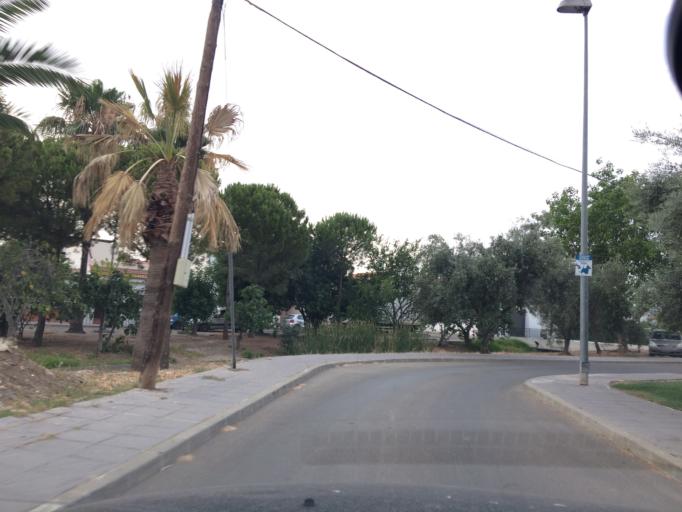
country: ES
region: Andalusia
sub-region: Provincia de Malaga
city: Estacion de Cartama
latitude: 36.7297
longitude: -4.5718
